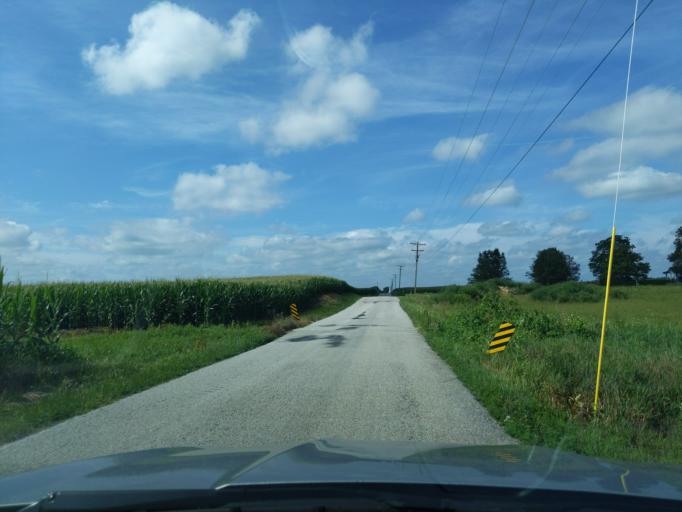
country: US
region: Indiana
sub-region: Ripley County
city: Batesville
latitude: 39.2698
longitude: -85.3476
